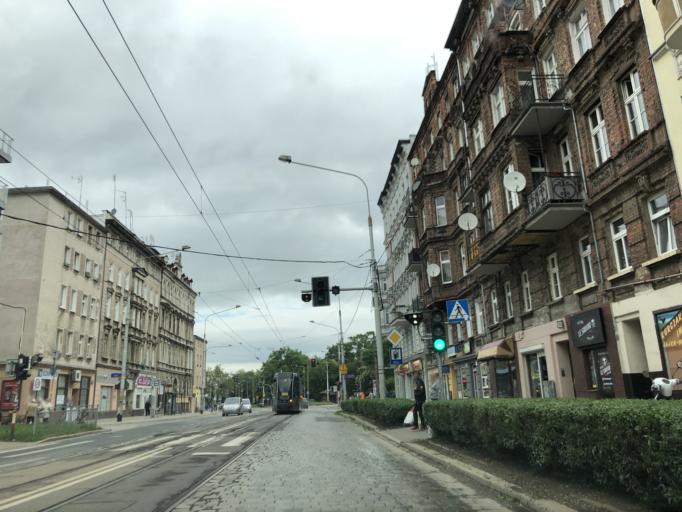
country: PL
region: Lower Silesian Voivodeship
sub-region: Powiat wroclawski
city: Wroclaw
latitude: 51.1213
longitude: 17.0310
